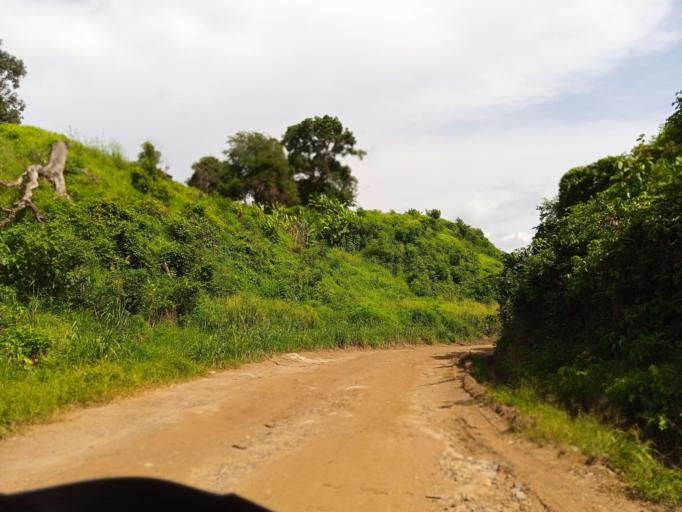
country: SL
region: Northern Province
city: Tintafor
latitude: 8.6122
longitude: -13.2083
